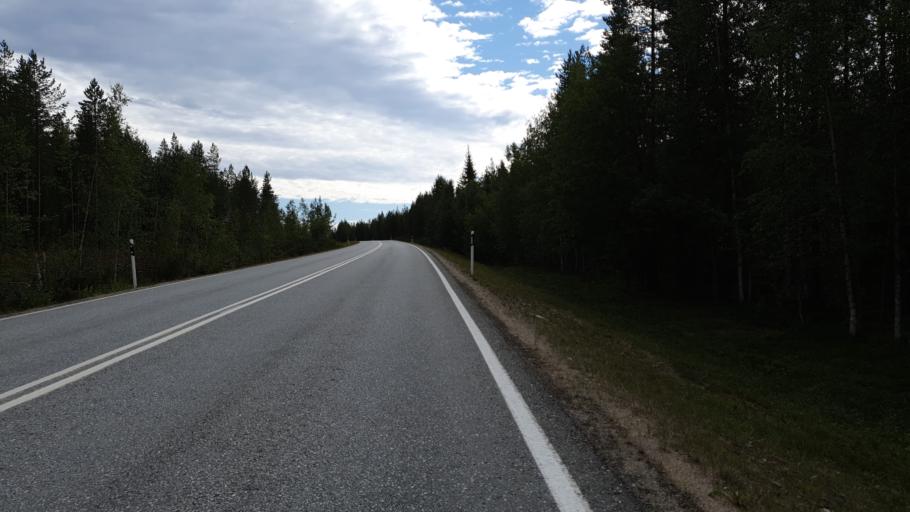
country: FI
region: Kainuu
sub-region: Kehys-Kainuu
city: Kuhmo
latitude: 64.4904
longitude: 29.8545
